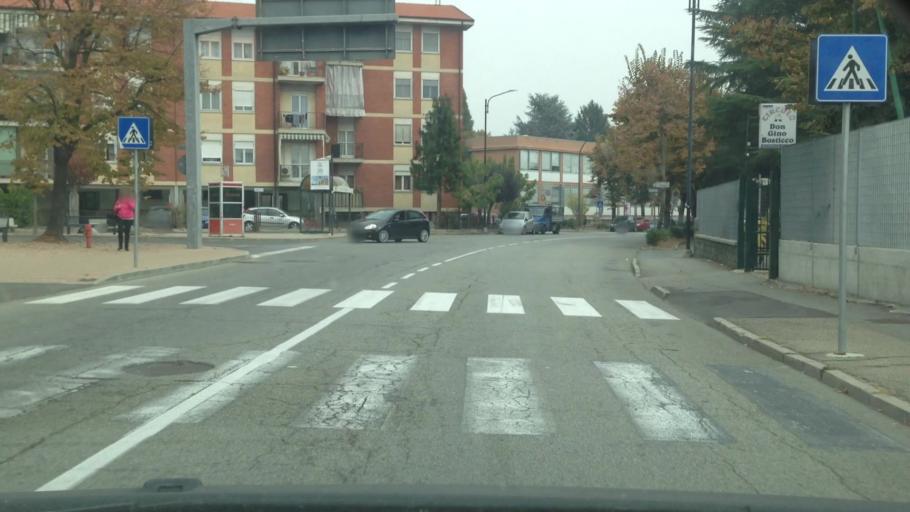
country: IT
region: Piedmont
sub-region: Provincia di Asti
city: Asti
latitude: 44.9073
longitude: 8.1886
